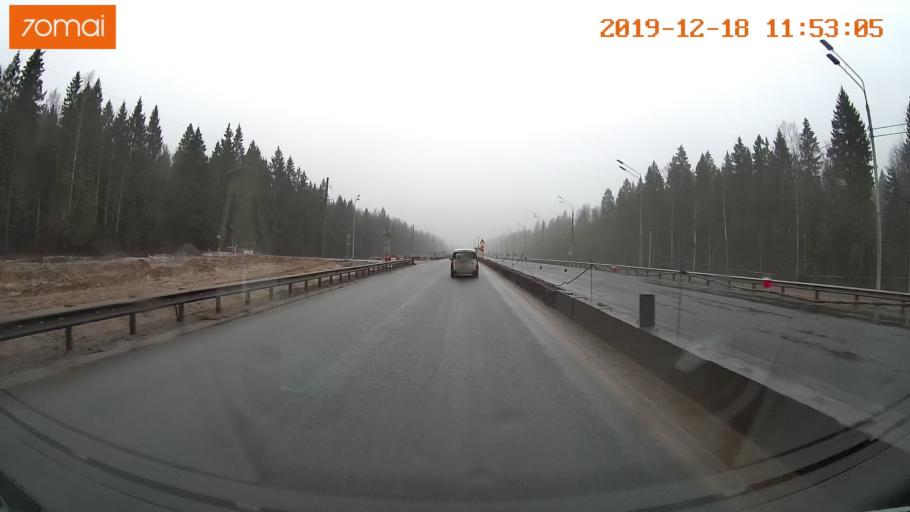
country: RU
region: Moskovskaya
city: Yershovo
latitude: 55.8008
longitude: 36.9207
